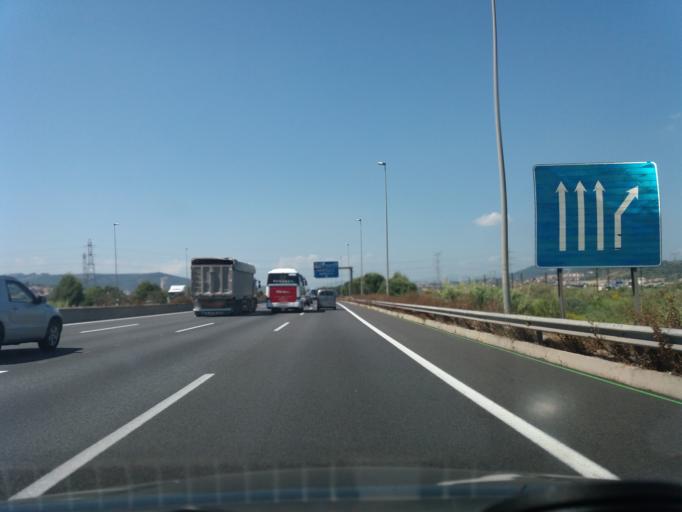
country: ES
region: Catalonia
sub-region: Provincia de Barcelona
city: Santa Coloma de Cervello
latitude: 41.3819
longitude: 2.0239
